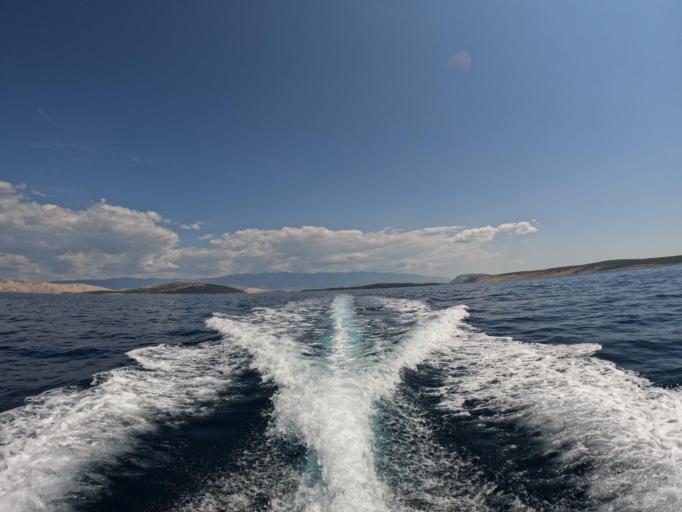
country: HR
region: Primorsko-Goranska
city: Lopar
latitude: 44.8650
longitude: 14.6854
